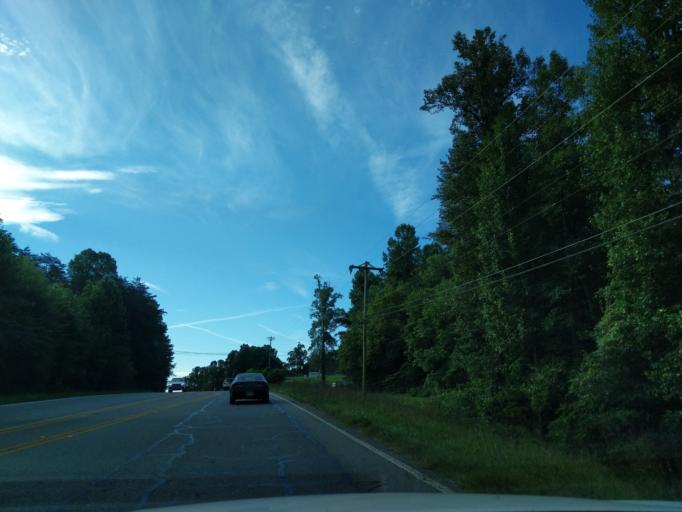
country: US
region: Georgia
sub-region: Fannin County
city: Blue Ridge
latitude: 34.9047
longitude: -84.3746
